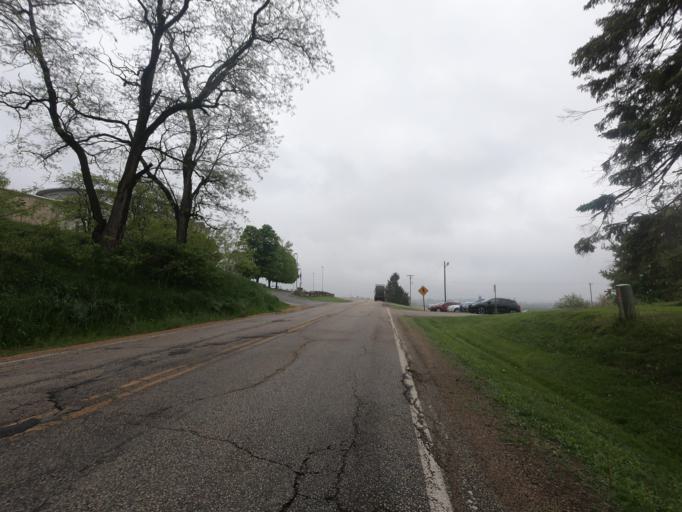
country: US
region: Illinois
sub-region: Jo Daviess County
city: East Dubuque
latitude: 42.5227
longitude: -90.5418
